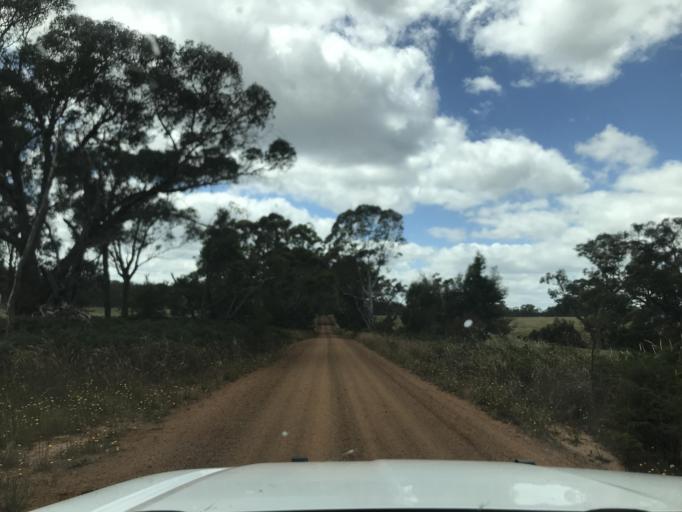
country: AU
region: South Australia
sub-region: Wattle Range
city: Penola
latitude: -37.3716
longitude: 141.2303
